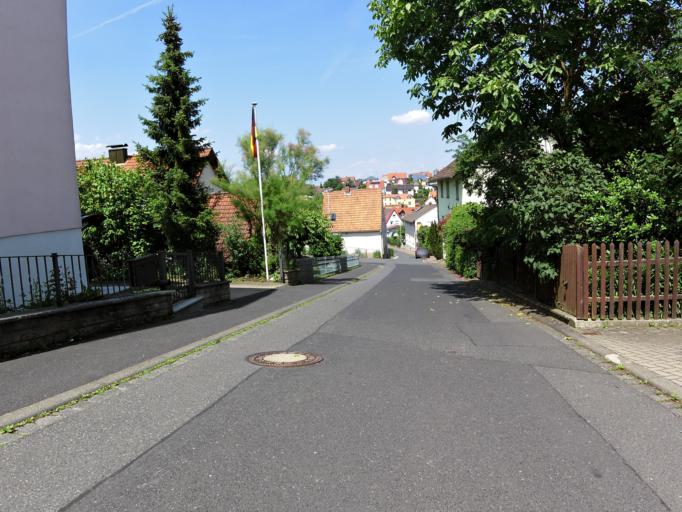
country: DE
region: Bavaria
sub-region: Regierungsbezirk Unterfranken
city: Eisingen
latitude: 49.7566
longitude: 9.8336
